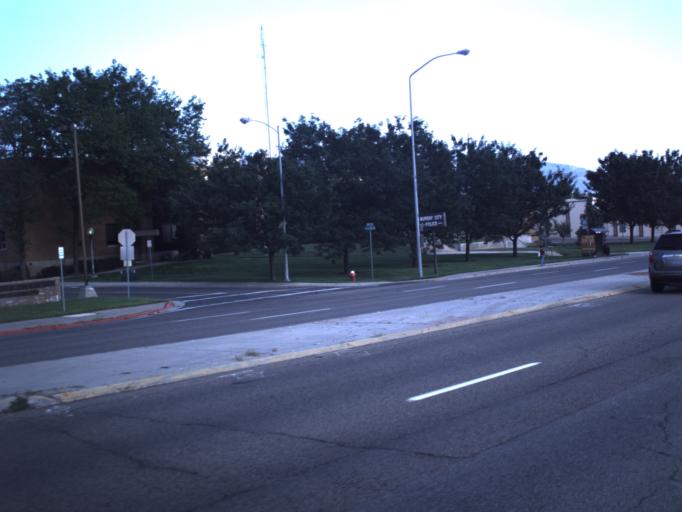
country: US
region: Utah
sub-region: Salt Lake County
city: Murray
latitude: 40.6632
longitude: -111.8884
